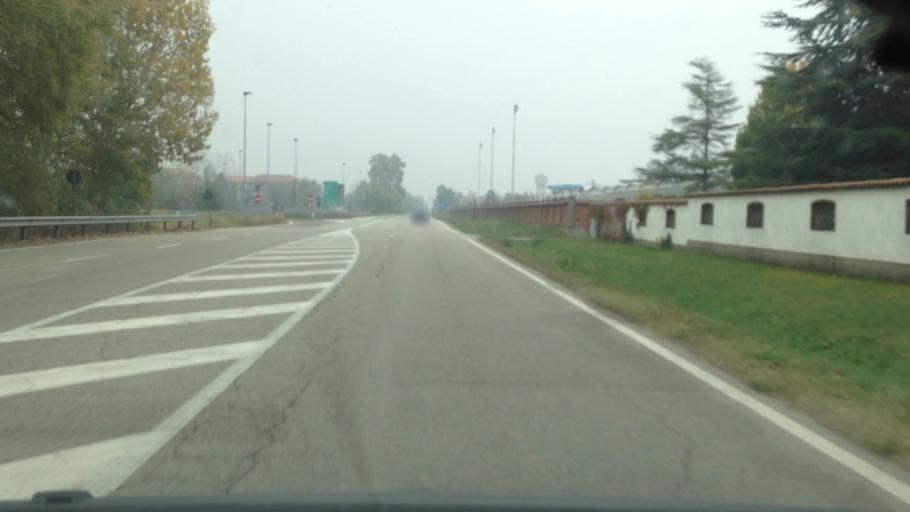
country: IT
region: Piedmont
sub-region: Provincia di Alessandria
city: Quattordio
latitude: 44.8995
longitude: 8.4192
